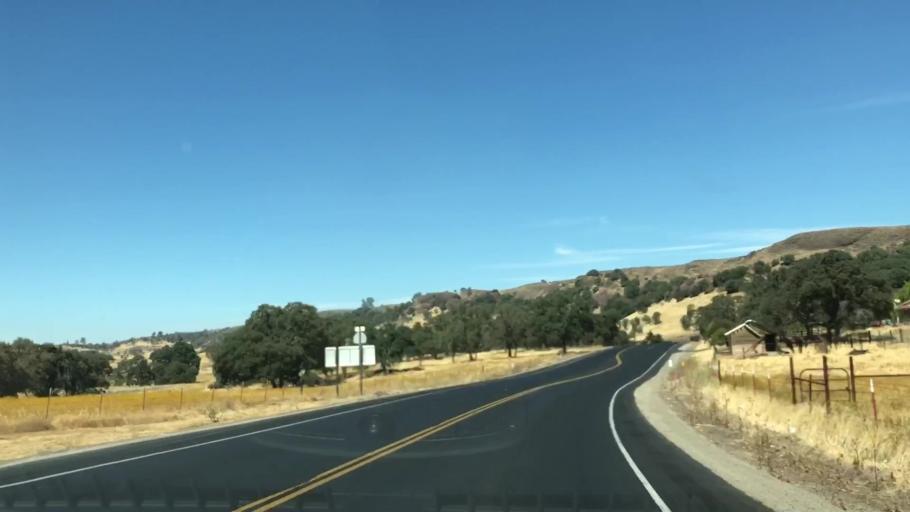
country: US
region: California
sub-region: Tuolumne County
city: Jamestown
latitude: 37.8864
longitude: -120.4850
